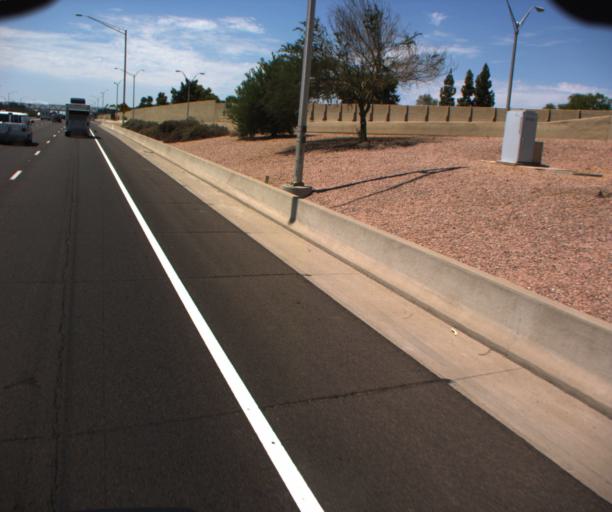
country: US
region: Arizona
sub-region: Maricopa County
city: Tempe
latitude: 33.3859
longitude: -111.8949
